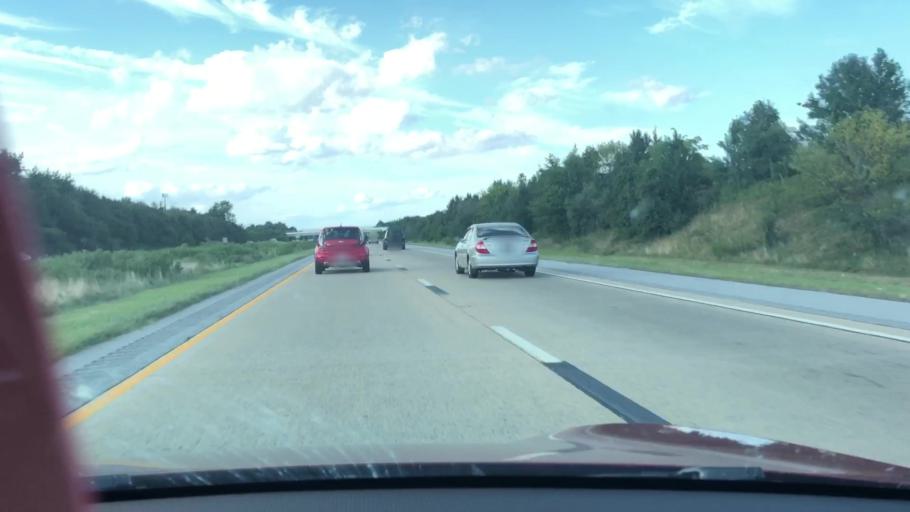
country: US
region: Delaware
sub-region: New Castle County
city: Middletown
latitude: 39.4884
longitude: -75.6481
